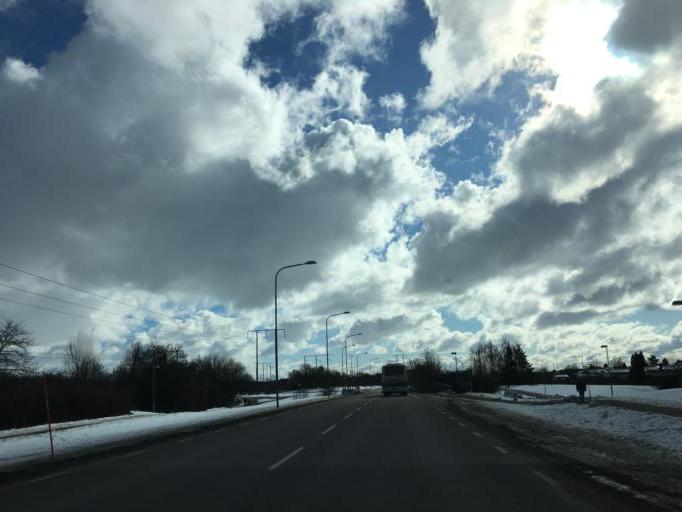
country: SE
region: Vaestmanland
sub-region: Vasteras
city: Vasteras
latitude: 59.5972
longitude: 16.4641
